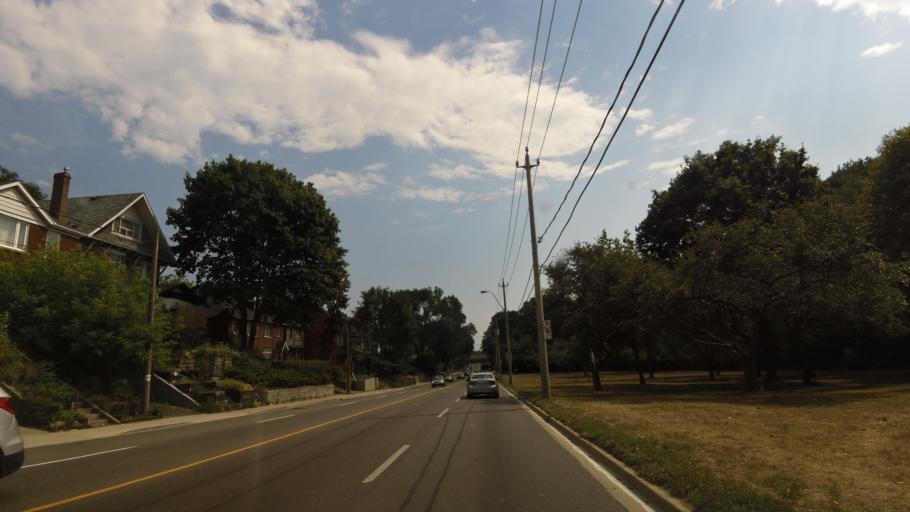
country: CA
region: Ontario
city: Toronto
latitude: 43.6426
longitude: -79.4554
